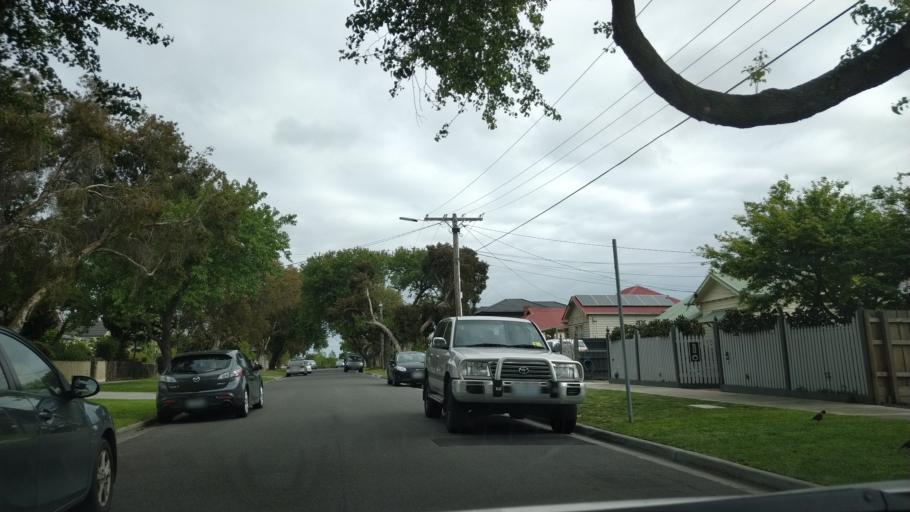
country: AU
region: Victoria
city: Hughesdale
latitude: -37.8987
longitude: 145.0815
